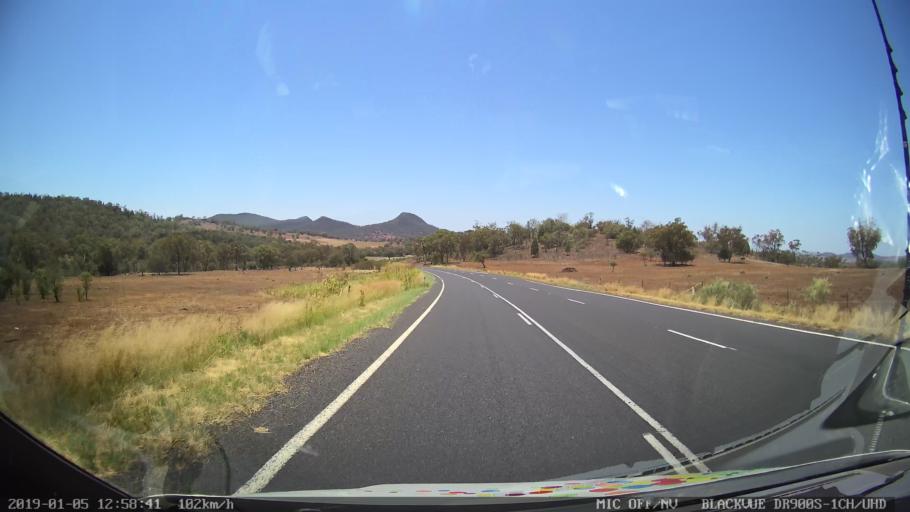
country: AU
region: New South Wales
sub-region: Narrabri
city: Boggabri
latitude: -31.1138
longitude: 149.7536
